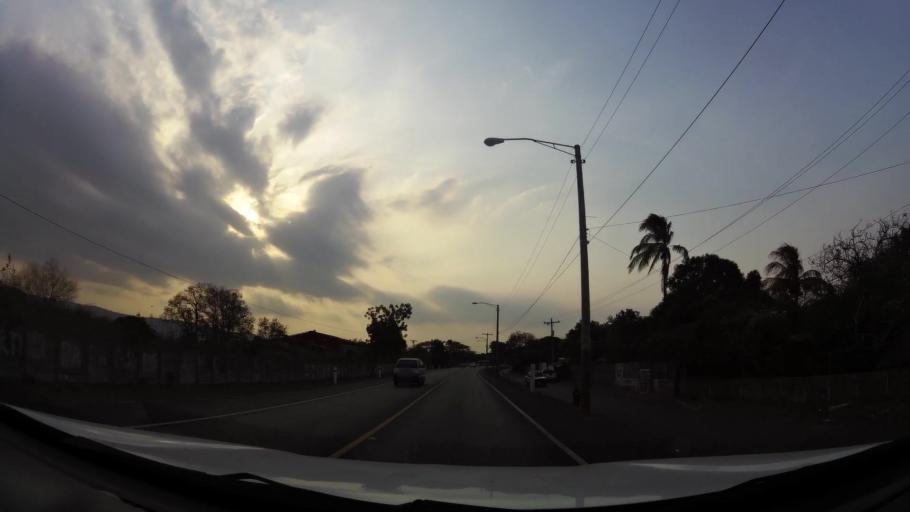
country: NI
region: Managua
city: Ciudad Sandino
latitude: 12.1895
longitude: -86.3665
